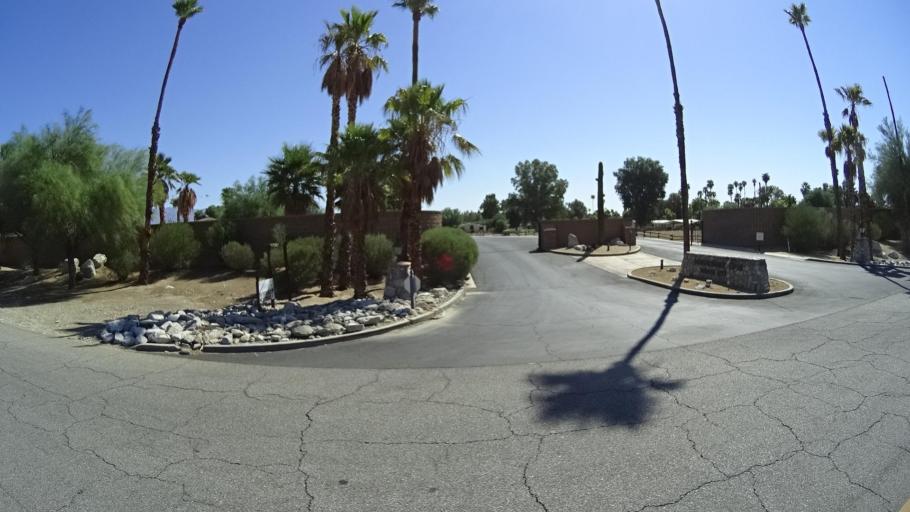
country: US
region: California
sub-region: San Diego County
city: Borrego Springs
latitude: 33.2633
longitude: -116.3661
